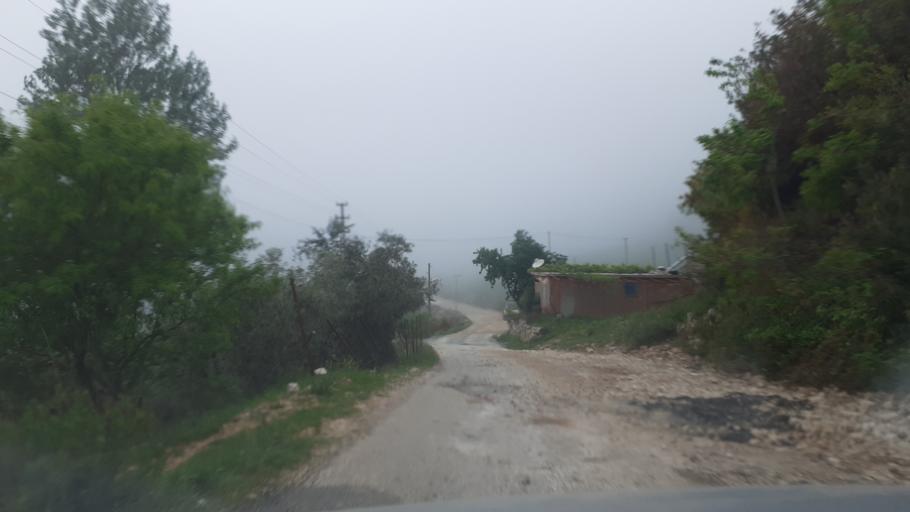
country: TR
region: Hatay
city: Yeditepe
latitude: 35.9709
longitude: 36.0035
